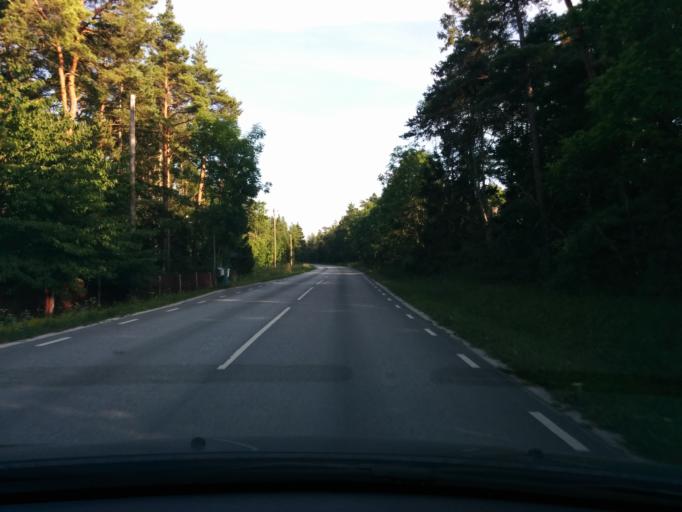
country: SE
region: Gotland
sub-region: Gotland
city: Visby
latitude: 57.5171
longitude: 18.5526
